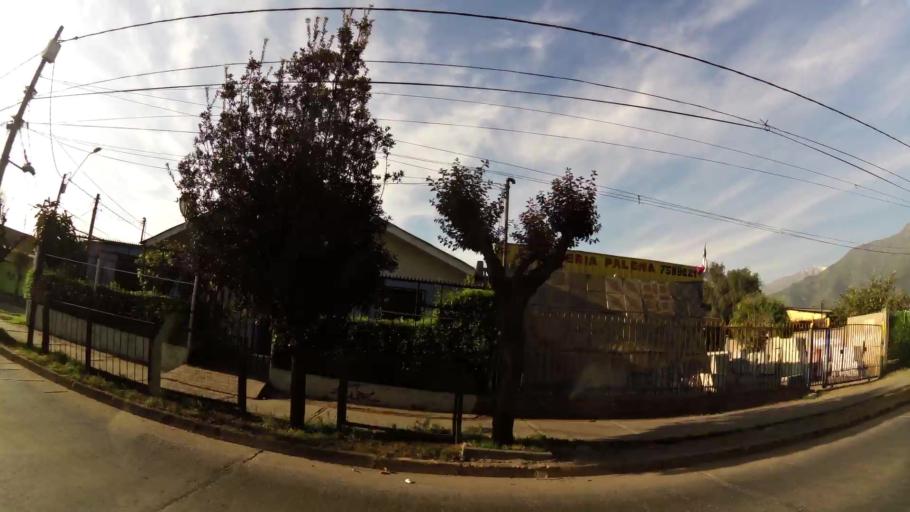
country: CL
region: Santiago Metropolitan
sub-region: Provincia de Santiago
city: Villa Presidente Frei, Nunoa, Santiago, Chile
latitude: -33.4747
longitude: -70.5485
